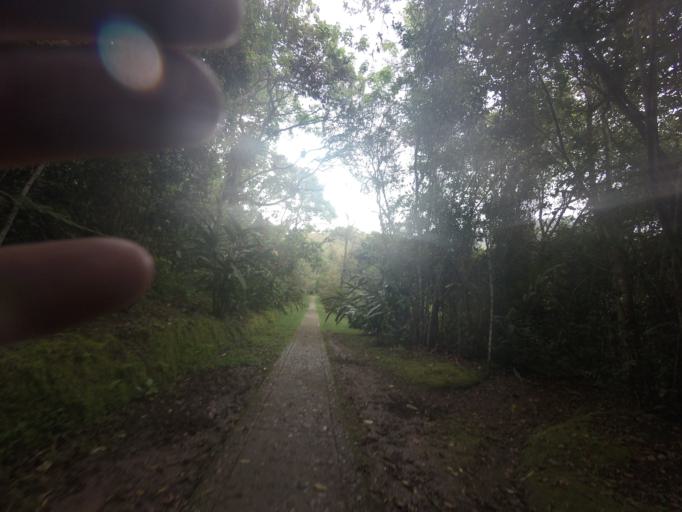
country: CO
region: Huila
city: Isnos
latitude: 1.9165
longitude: -76.2419
